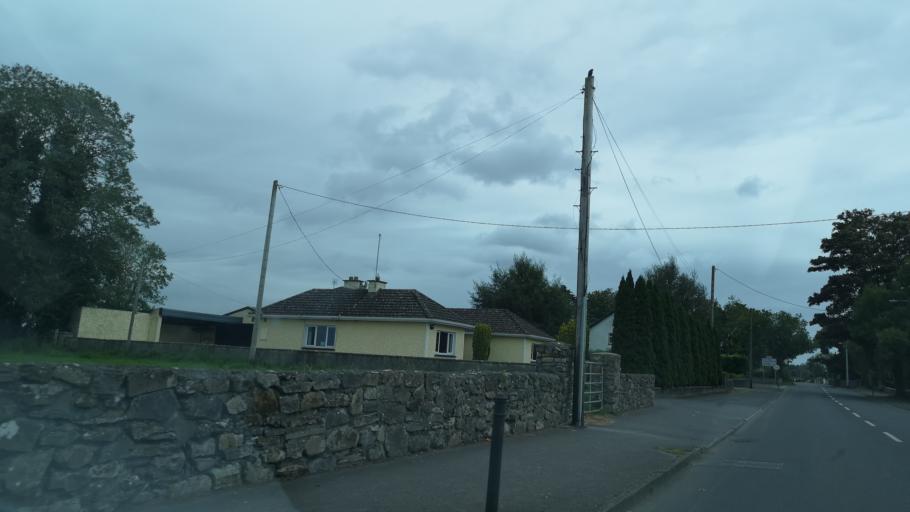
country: IE
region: Leinster
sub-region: Uibh Fhaili
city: Ferbane
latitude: 53.2247
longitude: -7.8792
